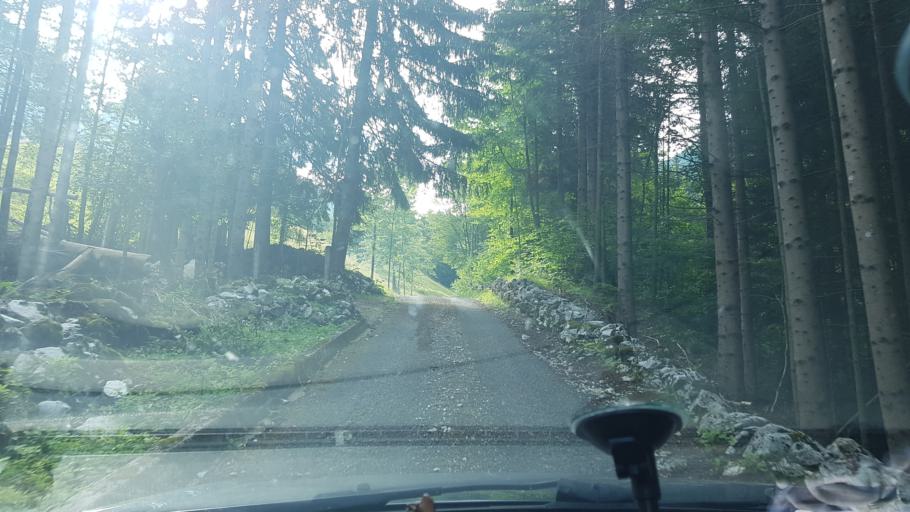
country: IT
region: Friuli Venezia Giulia
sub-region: Provincia di Udine
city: Prato
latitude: 46.3373
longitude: 13.4109
